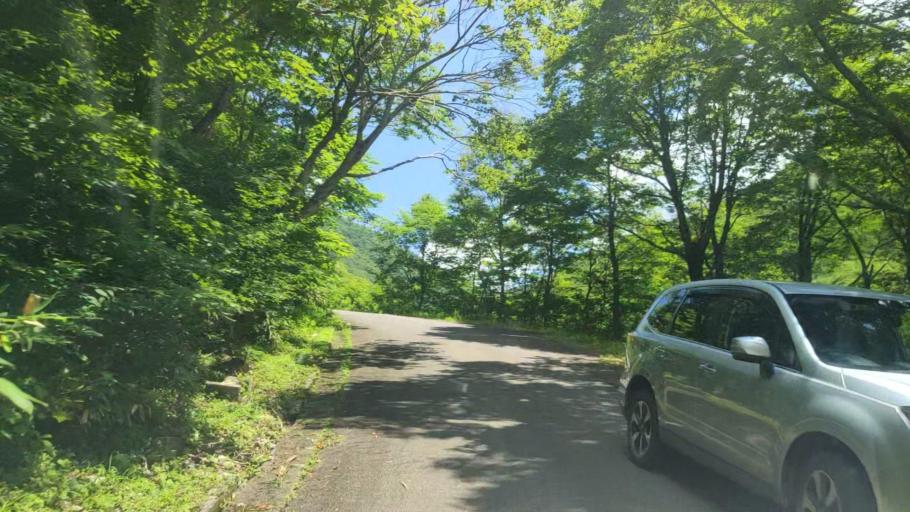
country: JP
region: Fukui
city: Ono
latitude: 35.7869
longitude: 136.5078
